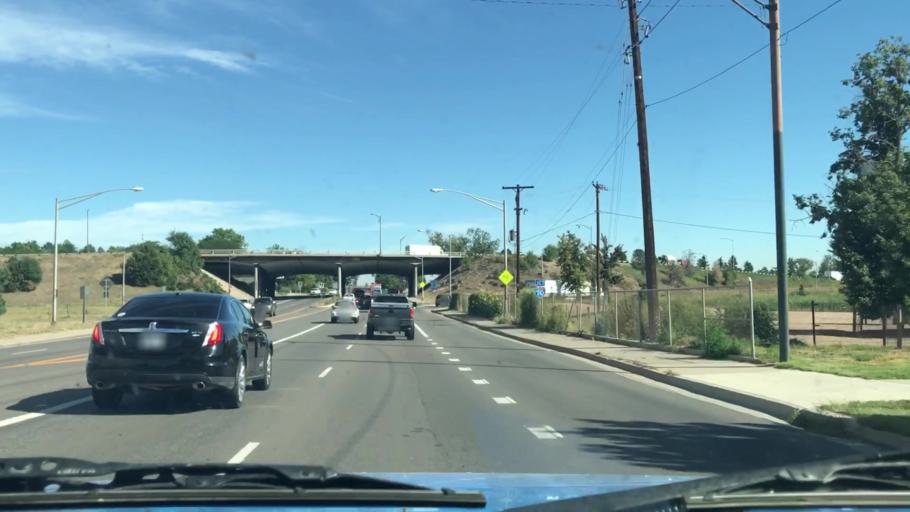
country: US
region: Colorado
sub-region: Jefferson County
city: Wheat Ridge
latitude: 39.7818
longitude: -105.0532
